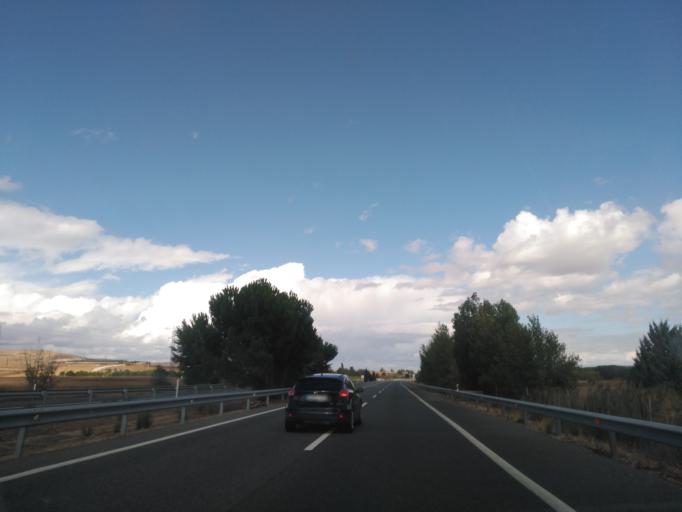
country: ES
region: Castille and Leon
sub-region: Provincia de Burgos
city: Villaldemiro
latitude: 42.2420
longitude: -3.9721
